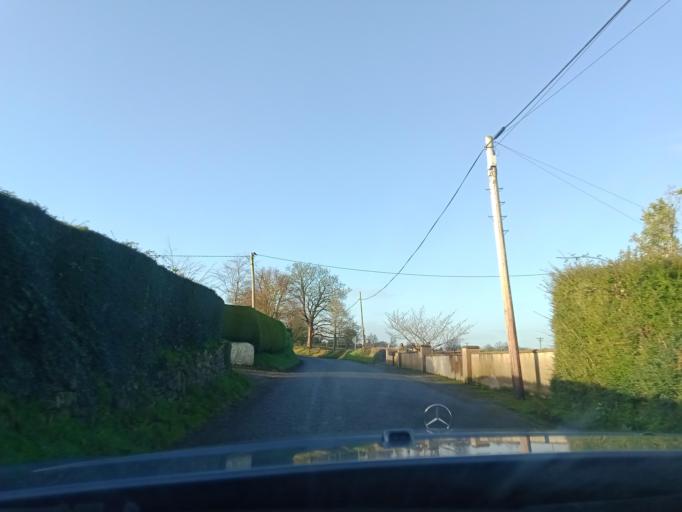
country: IE
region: Leinster
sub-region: Kilkenny
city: Callan
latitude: 52.4668
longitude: -7.4025
